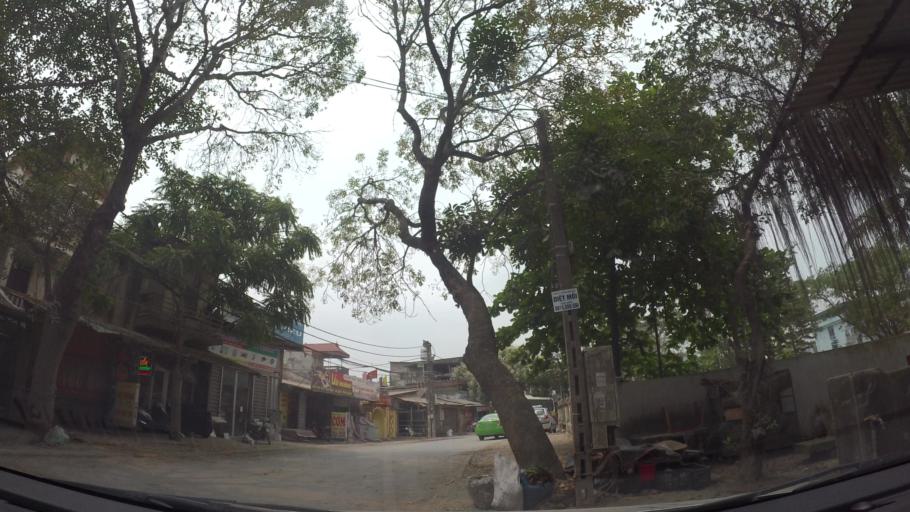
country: VN
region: Ha Noi
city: Cau Dien
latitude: 21.0295
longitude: 105.7400
